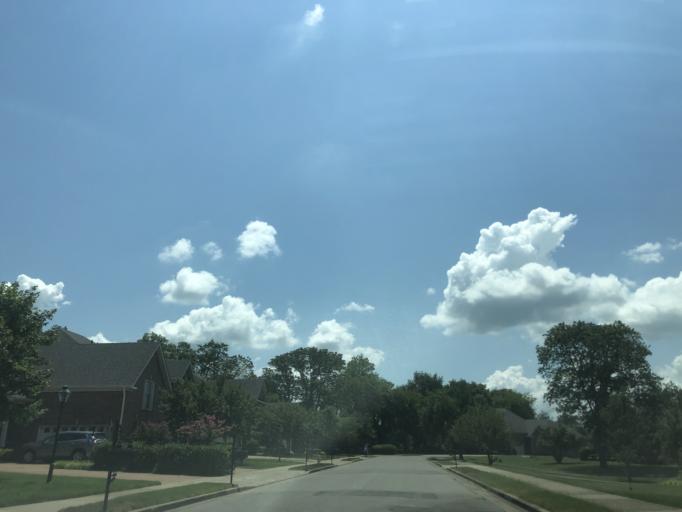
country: US
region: Tennessee
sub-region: Wilson County
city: Green Hill
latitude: 36.1947
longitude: -86.6013
